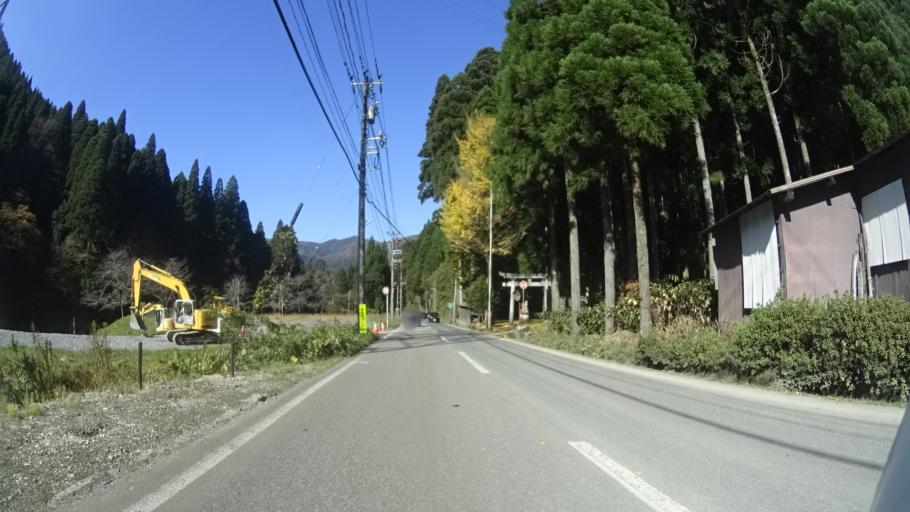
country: JP
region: Fukui
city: Ono
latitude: 35.9383
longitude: 136.3614
